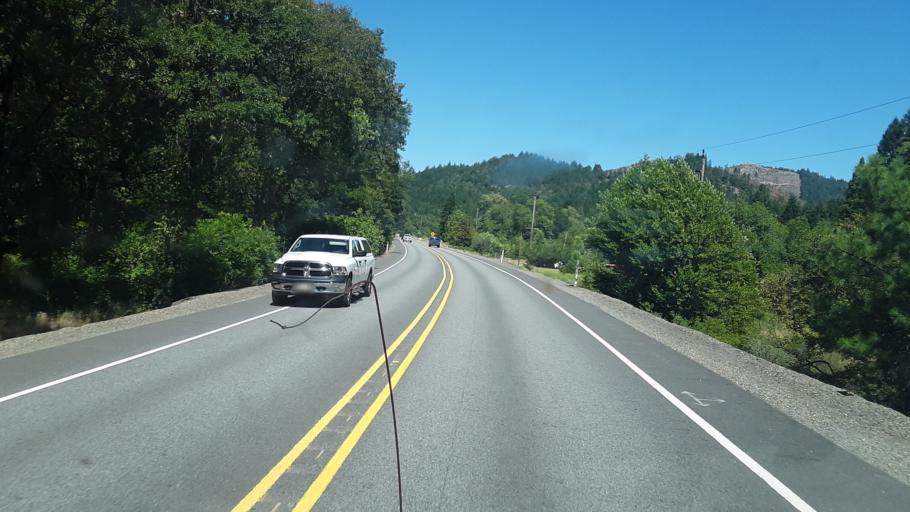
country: US
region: Oregon
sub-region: Josephine County
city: Redwood
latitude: 42.3626
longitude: -123.5174
